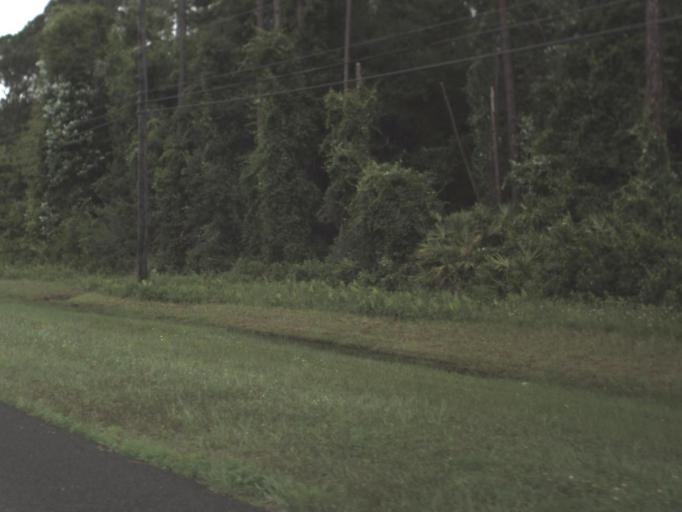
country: US
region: Florida
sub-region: Nassau County
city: Yulee
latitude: 30.6217
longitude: -81.6421
